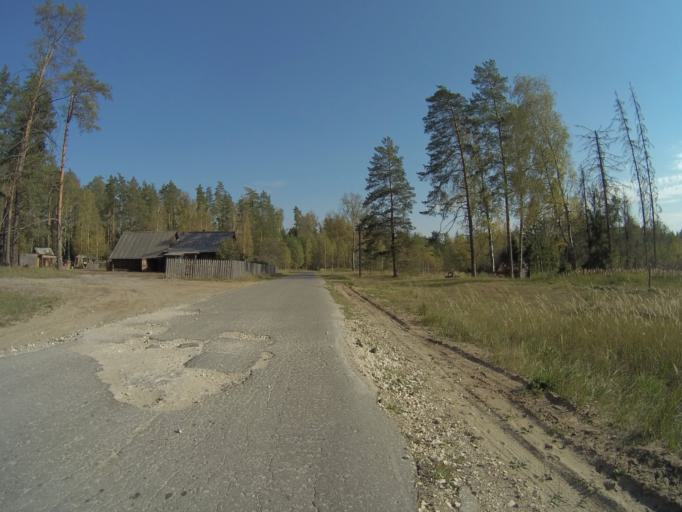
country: RU
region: Vladimir
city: Sobinka
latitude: 55.8621
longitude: 40.1533
